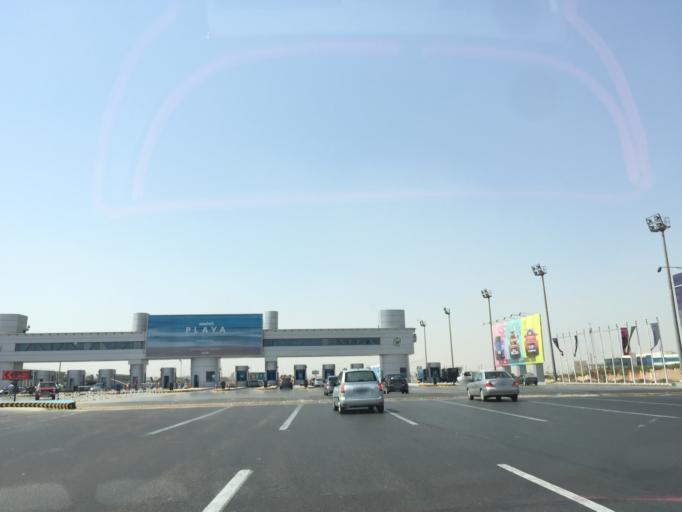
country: EG
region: Al Jizah
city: Awsim
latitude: 30.0700
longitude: 31.0141
